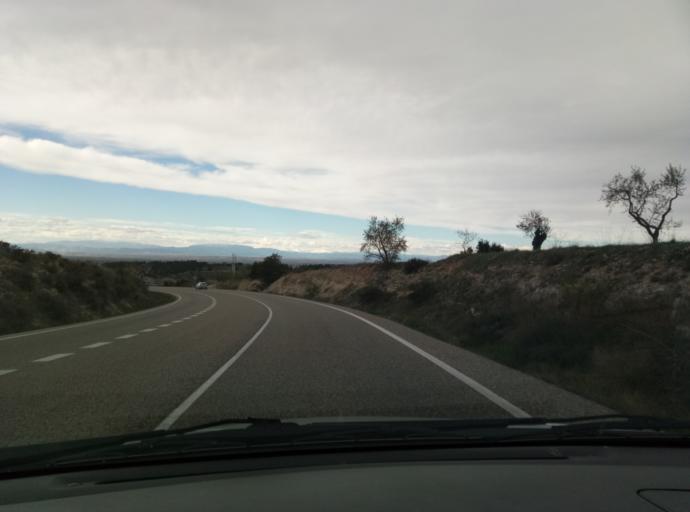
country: ES
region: Catalonia
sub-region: Provincia de Lleida
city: Ciutadilla
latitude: 41.5545
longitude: 1.1379
